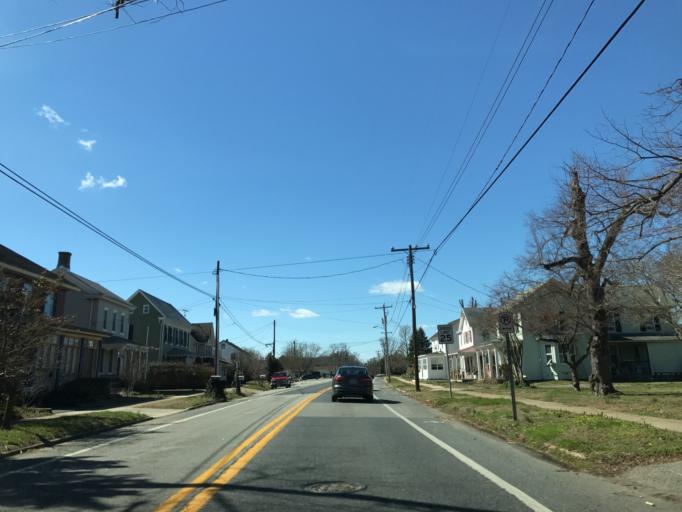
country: US
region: Delaware
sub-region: New Castle County
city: Townsend
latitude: 39.2592
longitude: -75.8414
